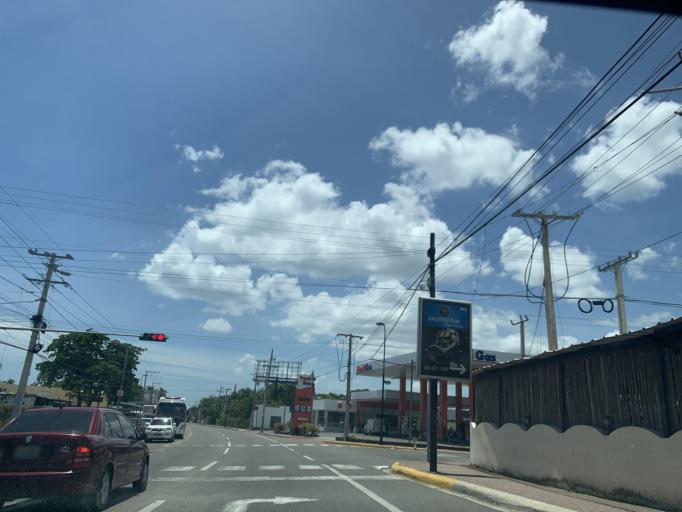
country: DO
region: Puerto Plata
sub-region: Puerto Plata
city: Puerto Plata
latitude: 19.7771
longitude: -70.6662
